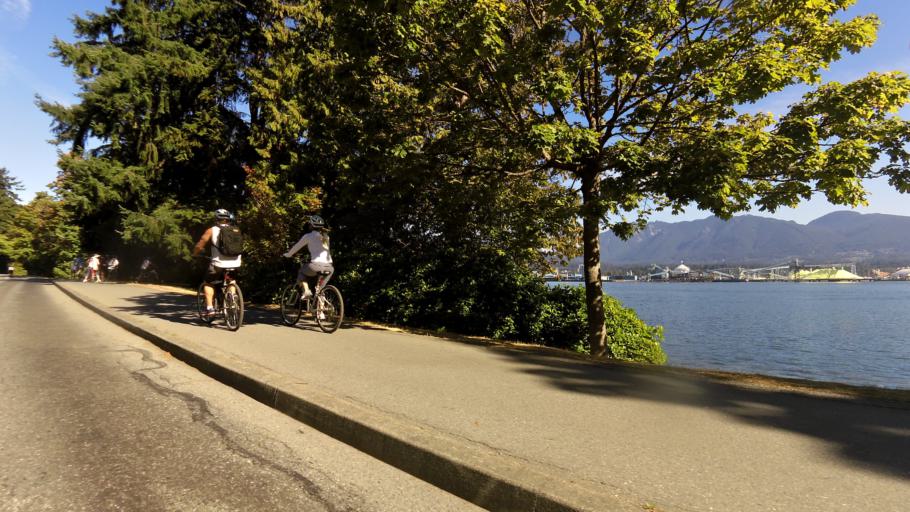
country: CA
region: British Columbia
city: West End
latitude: 49.2999
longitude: -123.1219
